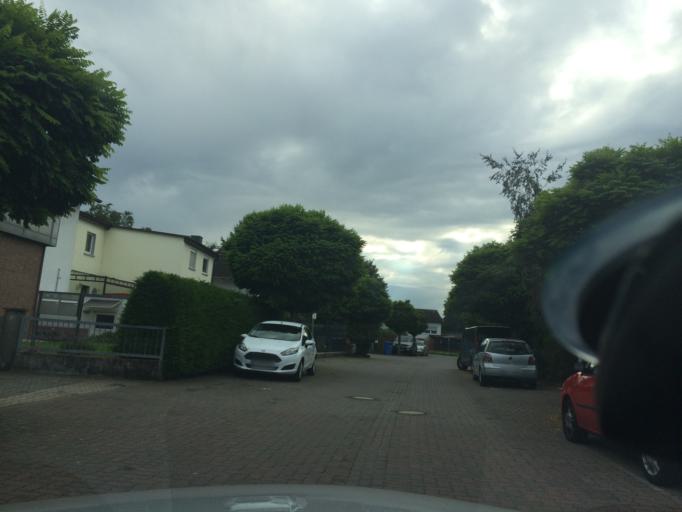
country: DE
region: Hesse
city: Morfelden-Walldorf
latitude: 49.9949
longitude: 8.5901
